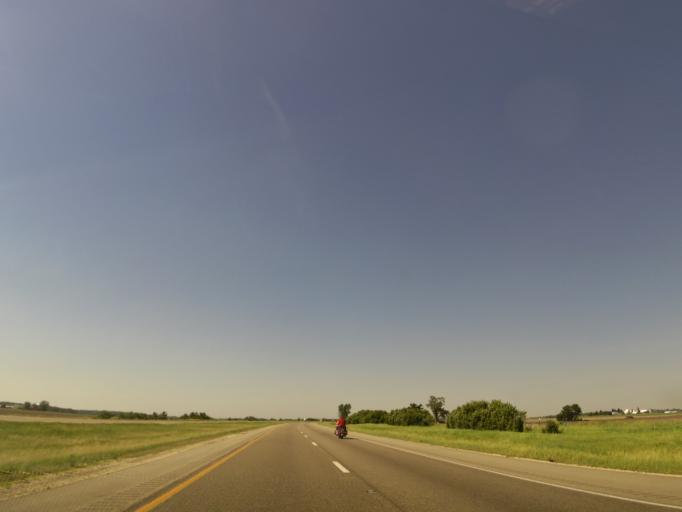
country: US
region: Illinois
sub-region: Ogle County
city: Davis Junction
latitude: 42.0670
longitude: -89.0217
